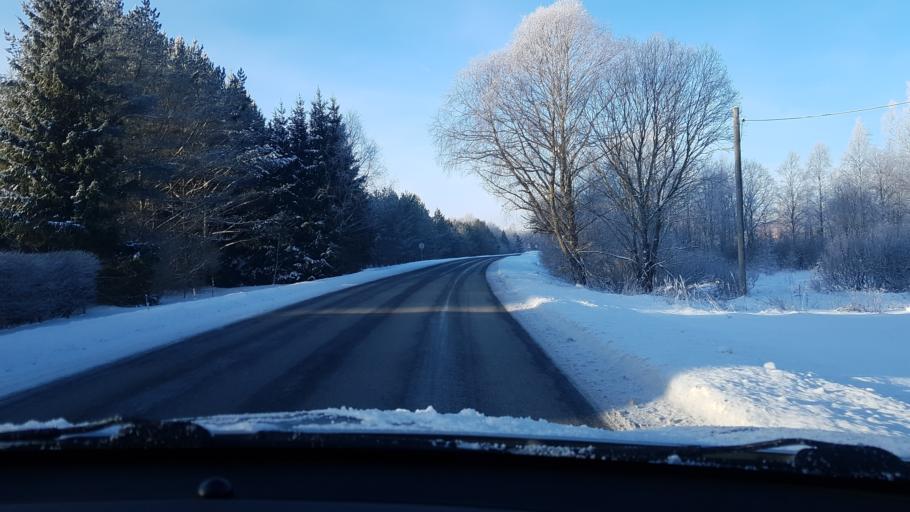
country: EE
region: Harju
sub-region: Keila linn
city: Keila
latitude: 59.3766
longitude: 24.4617
